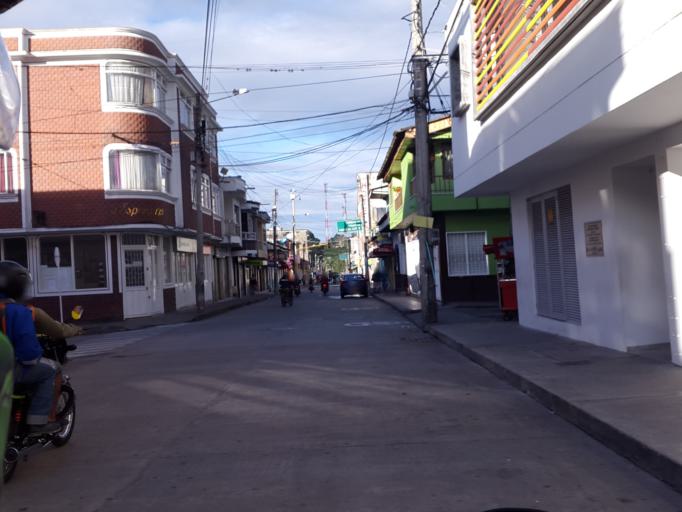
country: CO
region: Quindio
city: Montenegro
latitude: 4.5669
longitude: -75.7519
